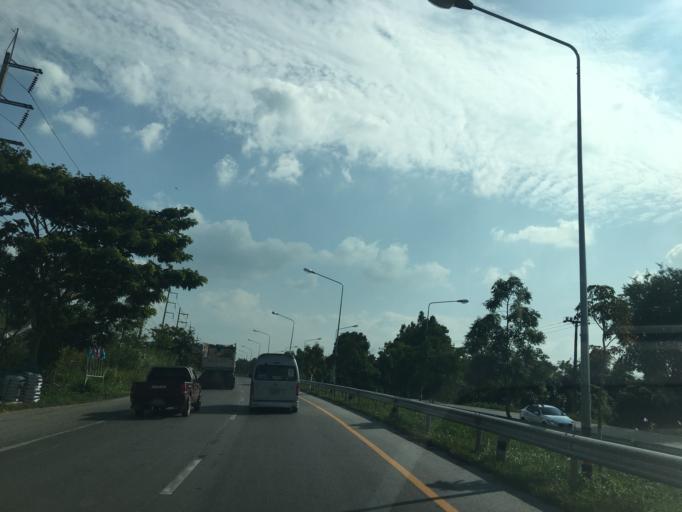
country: TH
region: Chiang Rai
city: Mae Lao
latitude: 19.7042
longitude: 99.7189
